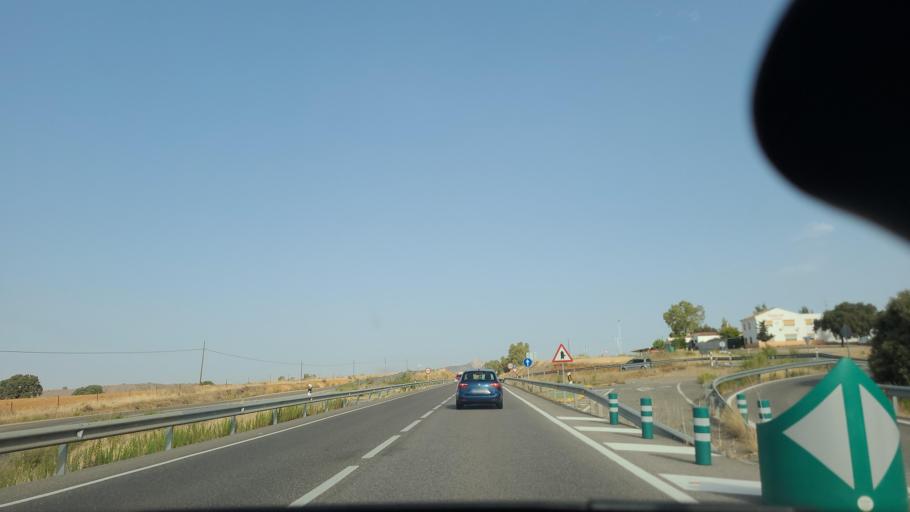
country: ES
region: Andalusia
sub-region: Province of Cordoba
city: Belmez
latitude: 38.2900
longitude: -5.2257
